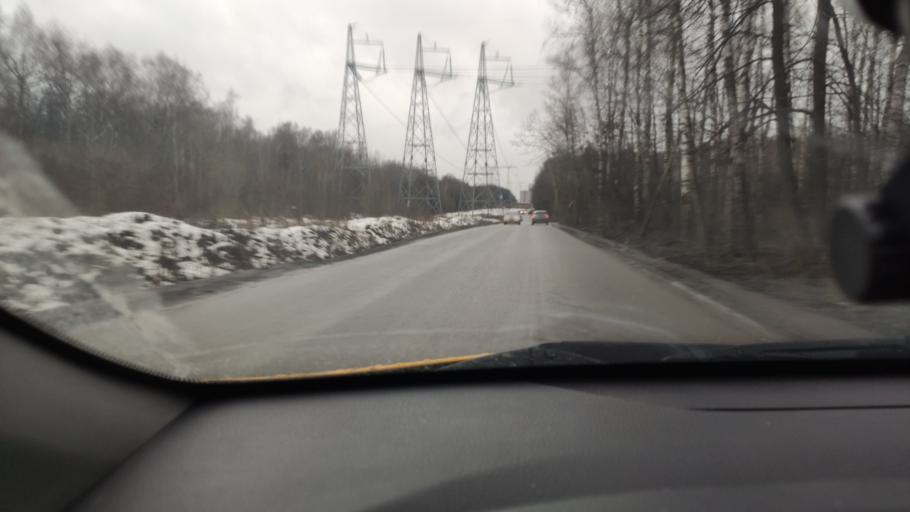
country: RU
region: Moscow
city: Annino
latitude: 55.5399
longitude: 37.6130
